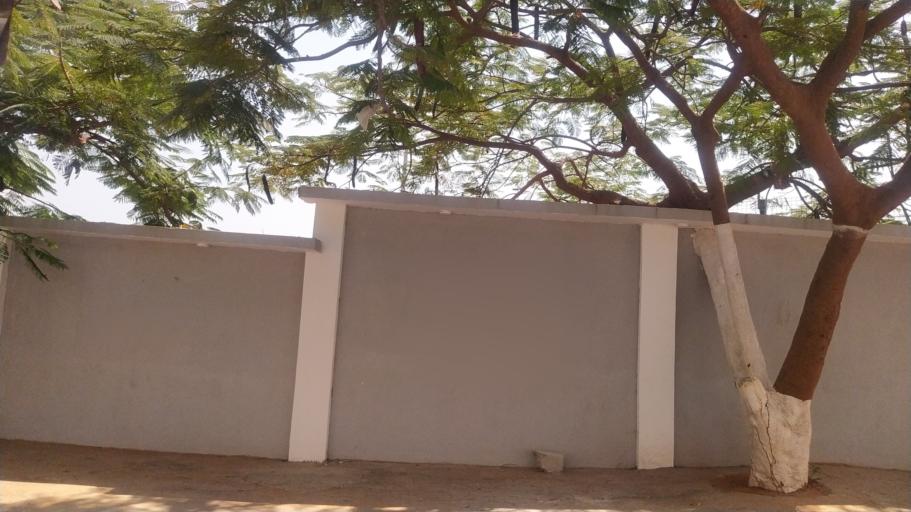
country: AO
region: Luanda
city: Luanda
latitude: -8.8984
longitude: 13.2270
